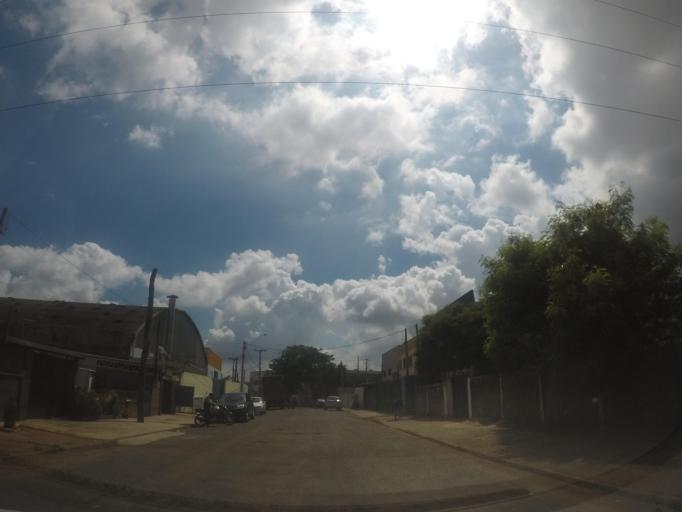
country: BR
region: Sao Paulo
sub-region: Hortolandia
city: Hortolandia
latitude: -22.8533
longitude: -47.1665
